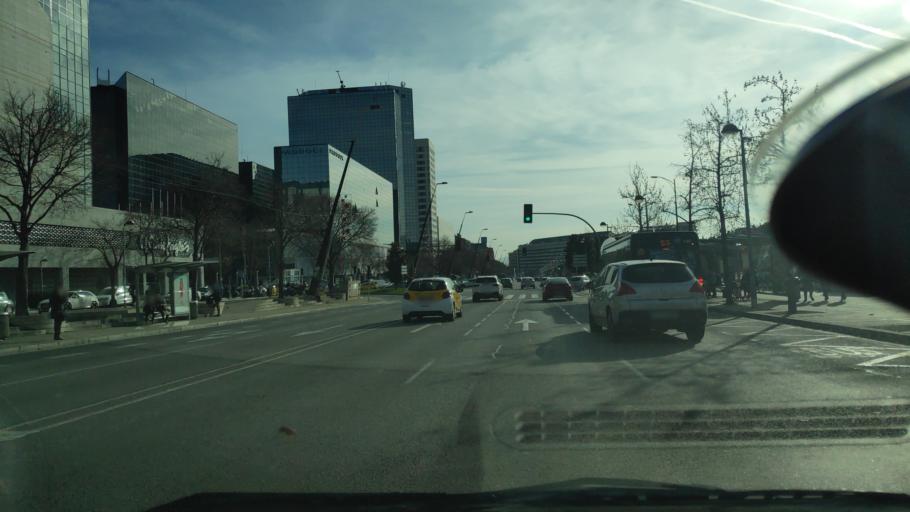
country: ES
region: Catalonia
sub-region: Provincia de Barcelona
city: Sabadell
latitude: 41.5548
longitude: 2.0975
